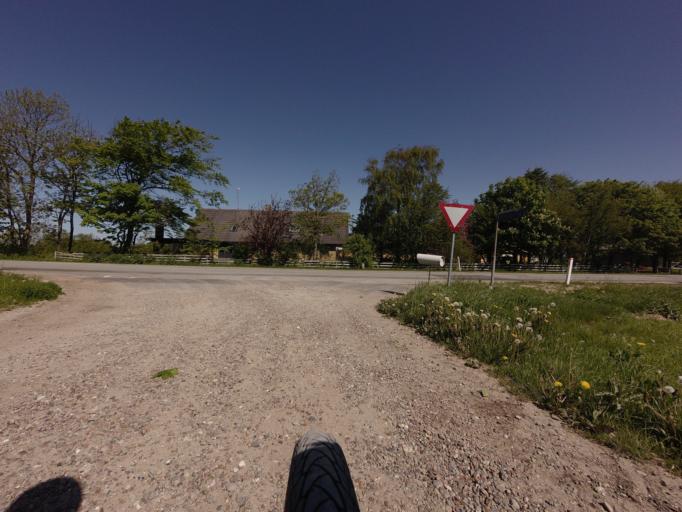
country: DK
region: North Denmark
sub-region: Hjorring Kommune
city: Hjorring
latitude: 57.4520
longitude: 9.8985
